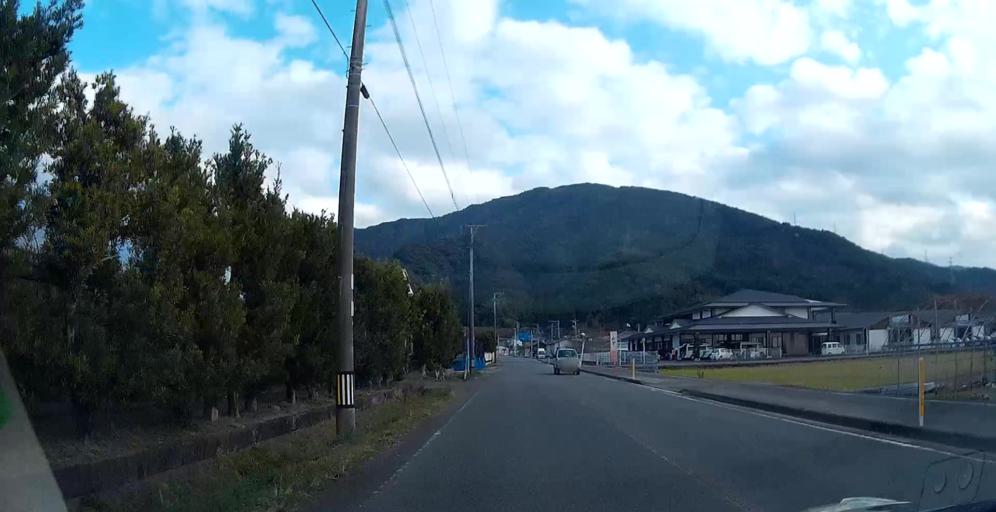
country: JP
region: Kumamoto
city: Yatsushiro
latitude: 32.5288
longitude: 130.6587
